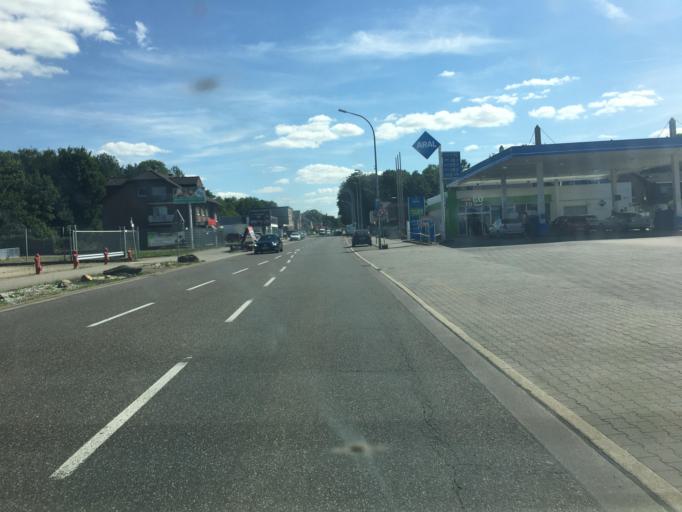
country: DE
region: North Rhine-Westphalia
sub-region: Regierungsbezirk Koln
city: Bergheim
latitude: 50.9869
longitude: 6.6720
